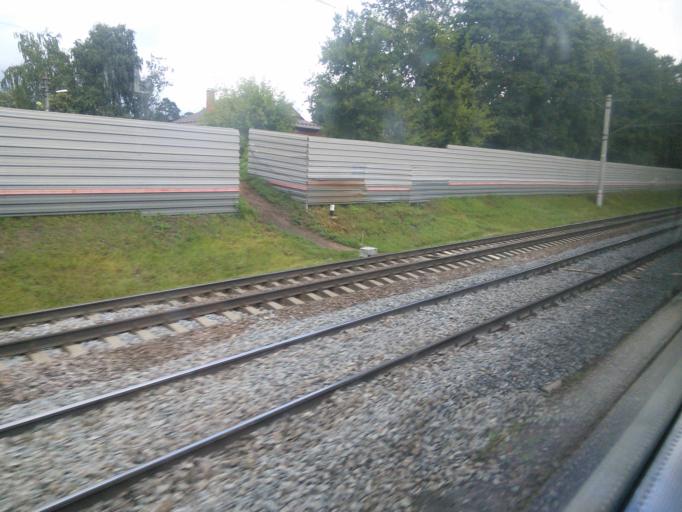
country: RU
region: Moskovskaya
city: Malakhovka
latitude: 55.6367
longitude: 38.0384
